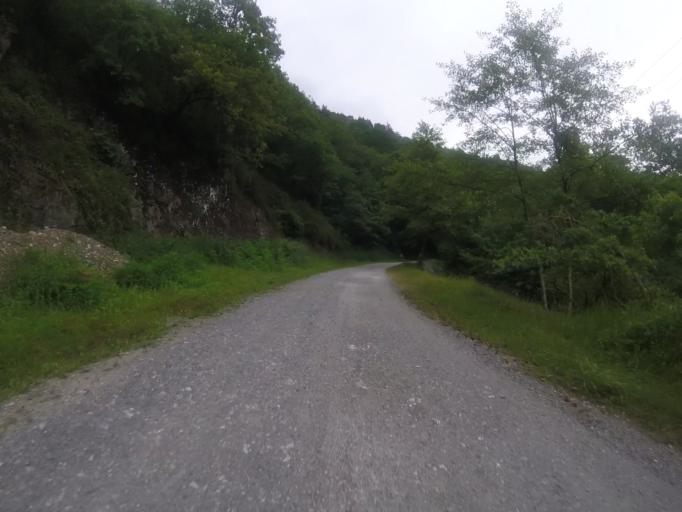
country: ES
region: Basque Country
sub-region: Provincia de Guipuzcoa
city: Berastegui
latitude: 43.1259
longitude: -1.9355
